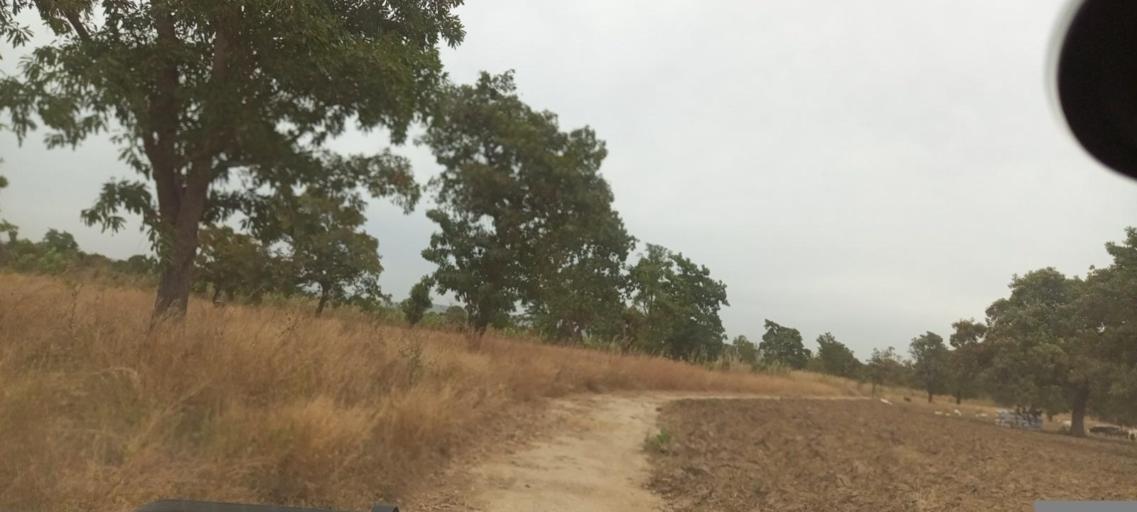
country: ML
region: Koulikoro
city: Kati
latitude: 12.7680
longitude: -8.3802
